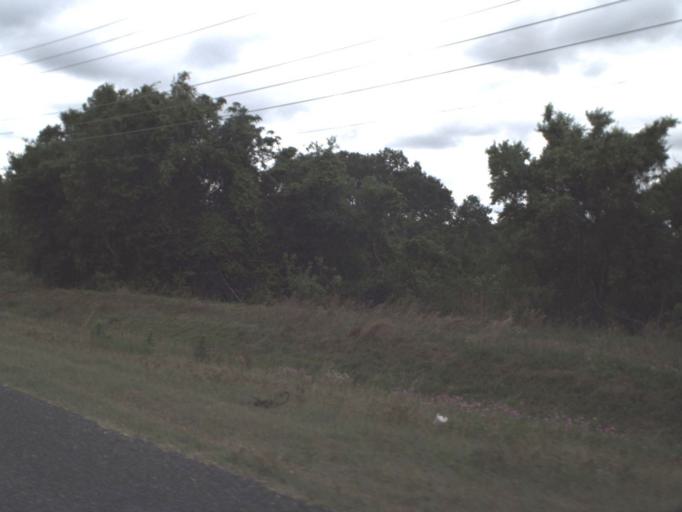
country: US
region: Florida
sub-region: Marion County
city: Ocala
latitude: 29.2666
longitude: -82.1754
